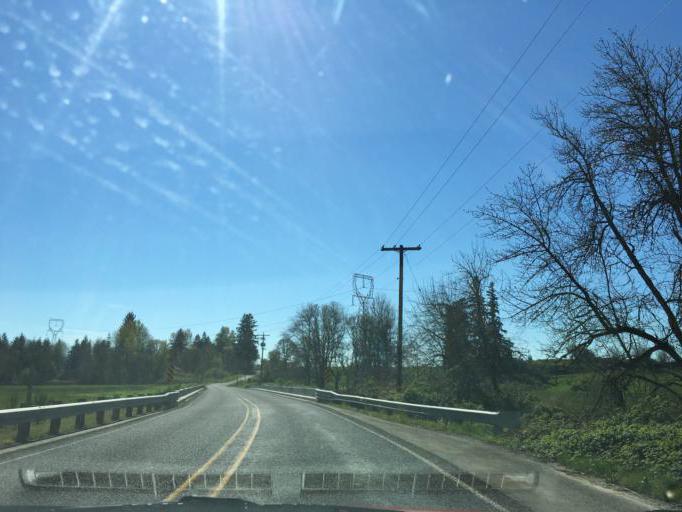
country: US
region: Oregon
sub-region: Marion County
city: Hubbard
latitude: 45.1527
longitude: -122.7231
